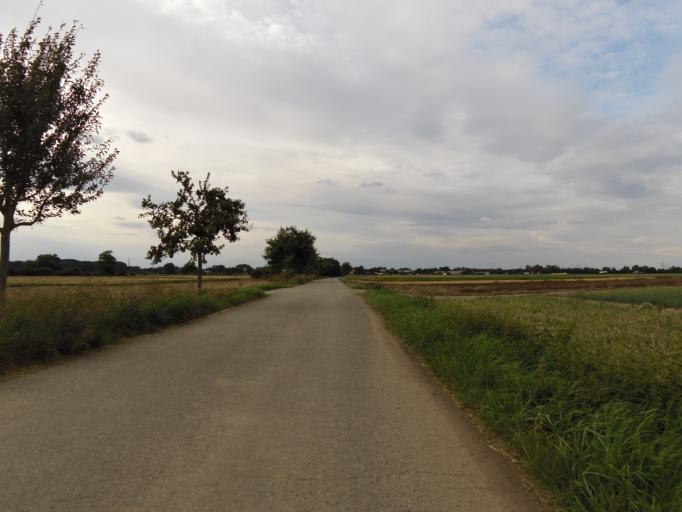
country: DE
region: Rheinland-Pfalz
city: Worms
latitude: 49.6253
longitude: 8.4043
